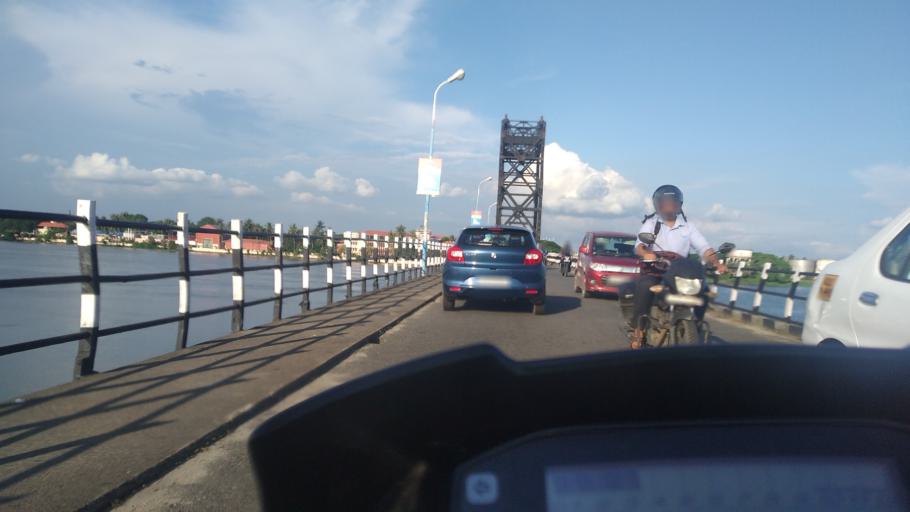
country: IN
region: Kerala
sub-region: Ernakulam
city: Cochin
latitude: 9.9366
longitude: 76.2655
